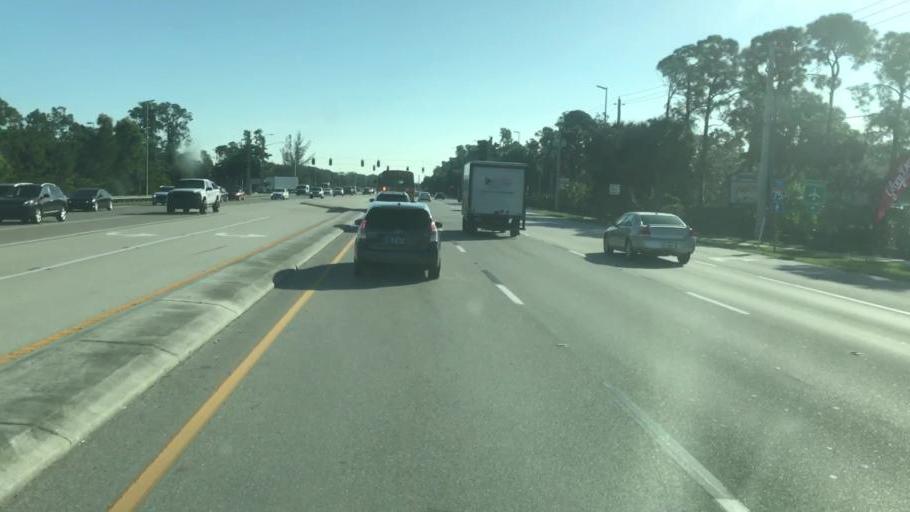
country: US
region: Florida
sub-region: Lee County
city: Villas
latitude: 26.5468
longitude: -81.8695
